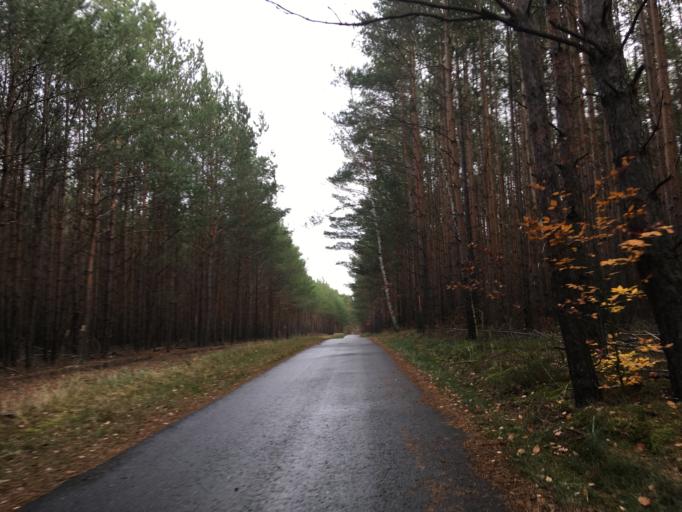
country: DE
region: Brandenburg
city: Tauer
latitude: 51.9192
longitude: 14.4846
